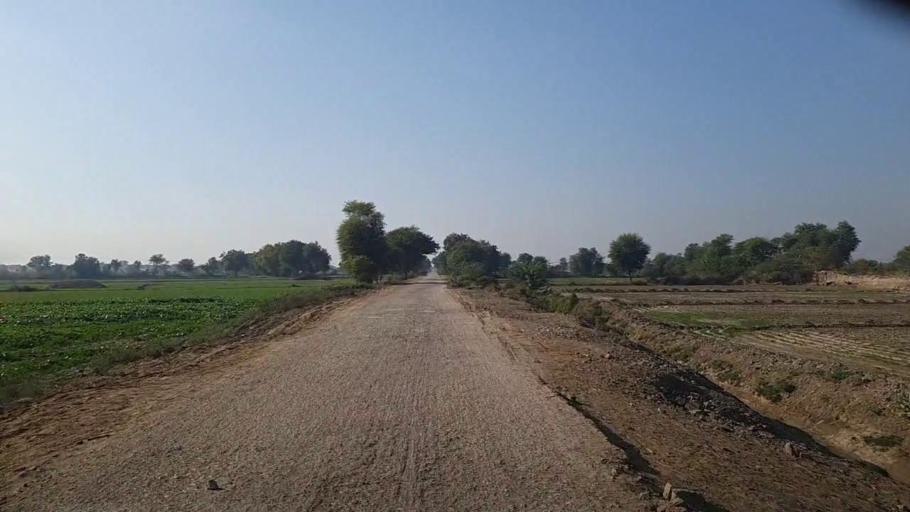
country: PK
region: Sindh
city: Darya Khan Marri
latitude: 26.6815
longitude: 68.3655
